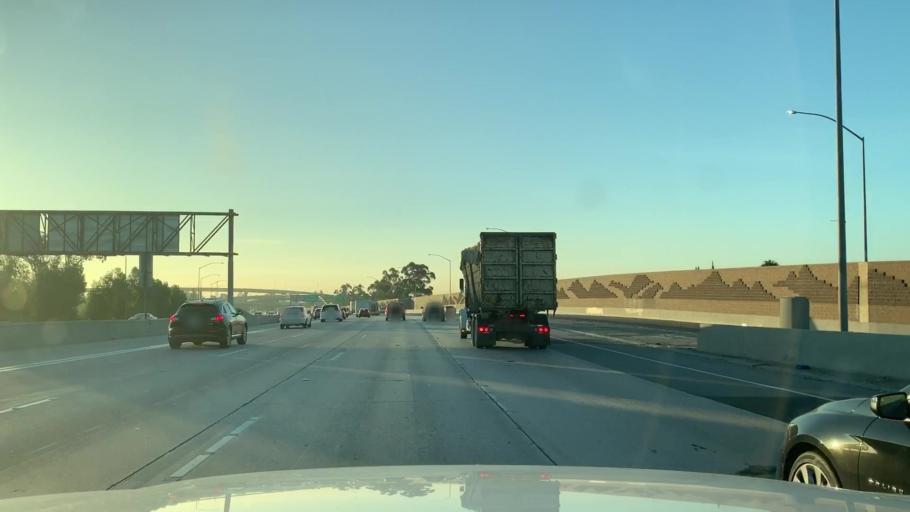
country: US
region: California
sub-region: Los Angeles County
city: San Fernando
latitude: 34.2719
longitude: -118.4487
